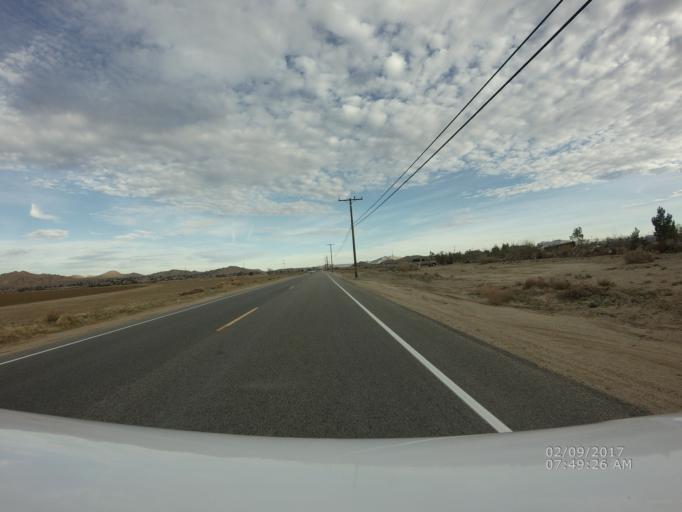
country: US
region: California
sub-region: Los Angeles County
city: Lake Los Angeles
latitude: 34.5772
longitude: -117.8266
